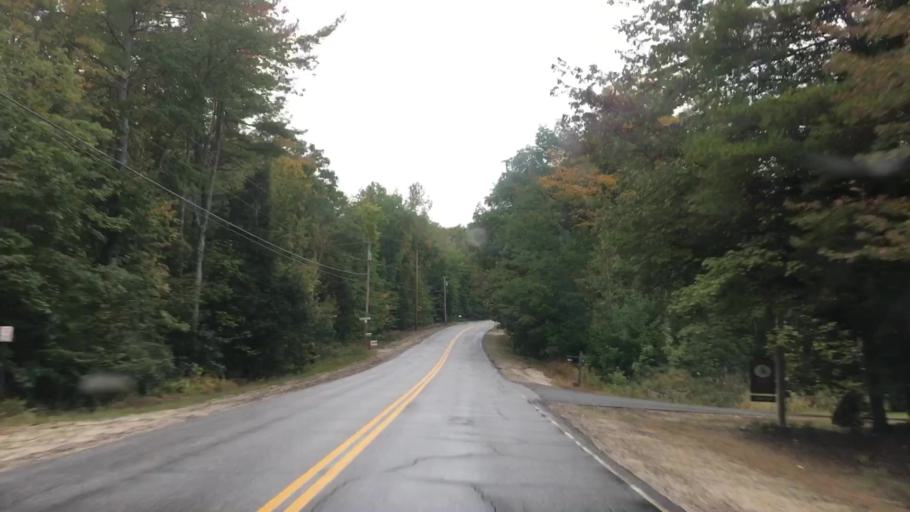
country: US
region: Maine
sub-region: Cumberland County
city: Raymond
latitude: 43.9343
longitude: -70.4182
